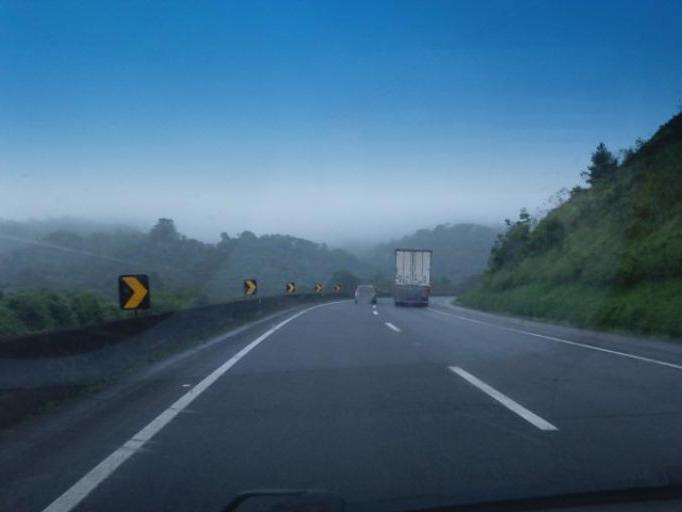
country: BR
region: Parana
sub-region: Antonina
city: Antonina
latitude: -25.0982
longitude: -48.6735
